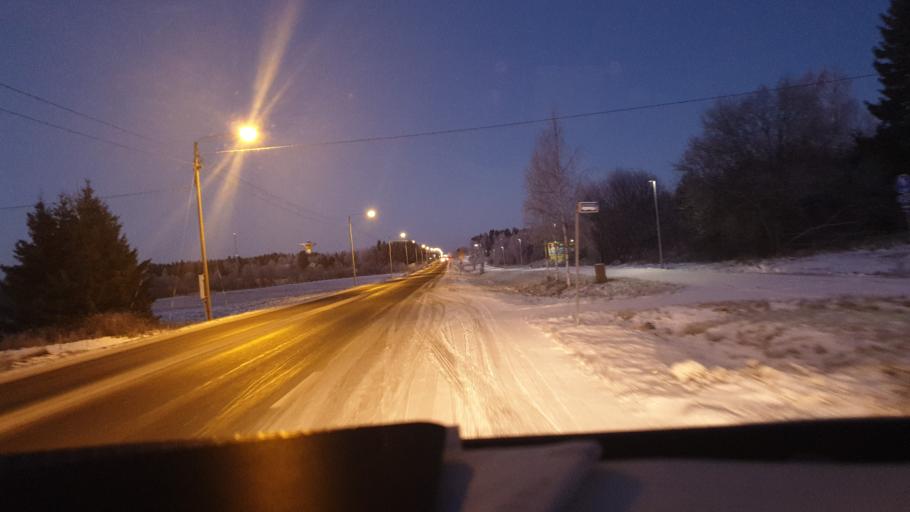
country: FI
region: Northern Ostrobothnia
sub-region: Raahe
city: Raahe
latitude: 64.6876
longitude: 24.5905
